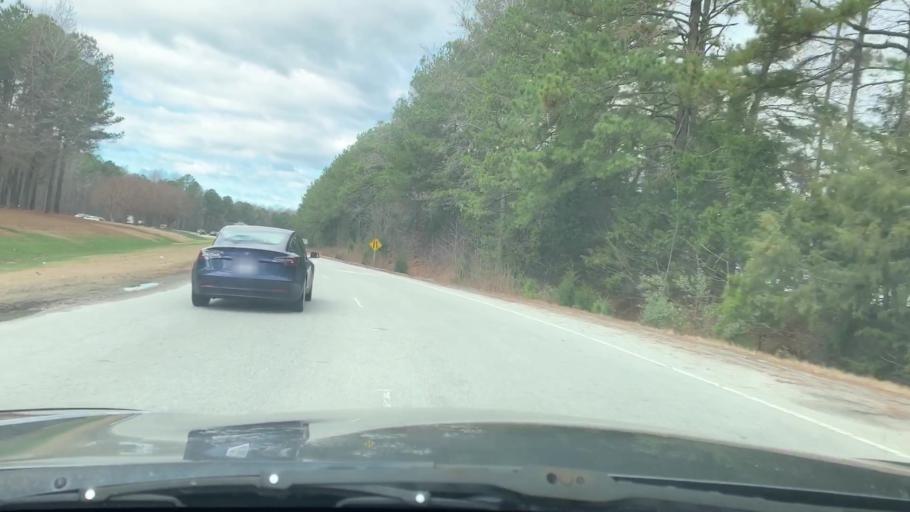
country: US
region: North Carolina
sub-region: Wake County
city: Cary
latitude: 35.8327
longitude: -78.7633
